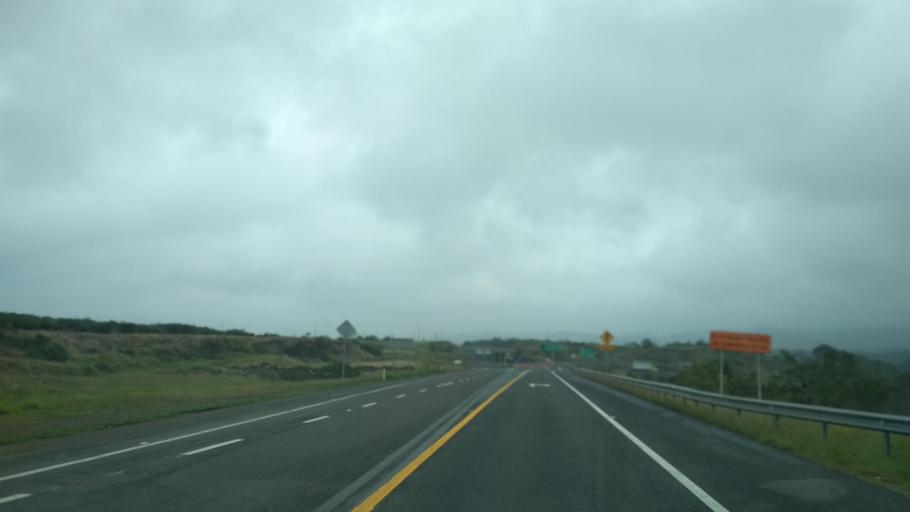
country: MX
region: Veracruz
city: Vega de San Marcos
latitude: 20.1514
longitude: -96.9492
